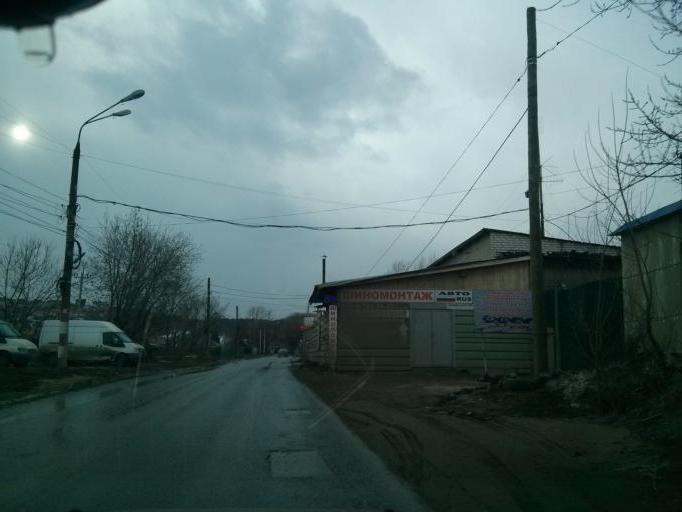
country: RU
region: Nizjnij Novgorod
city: Afonino
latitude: 56.2937
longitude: 44.1063
